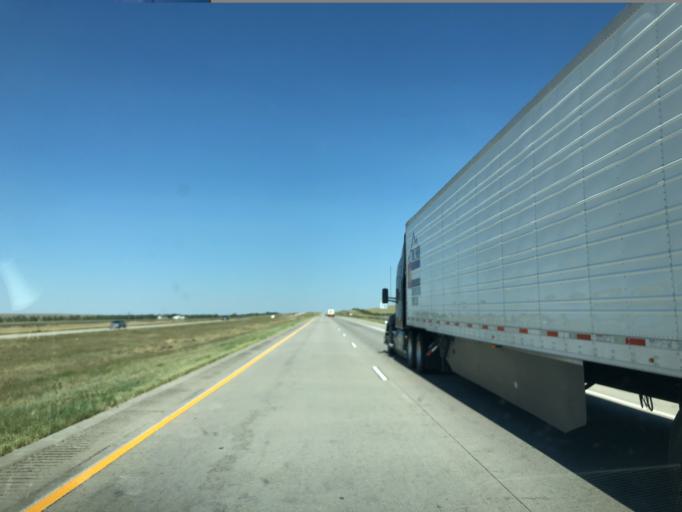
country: US
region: Colorado
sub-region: Lincoln County
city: Limon
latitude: 39.2778
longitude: -103.7547
